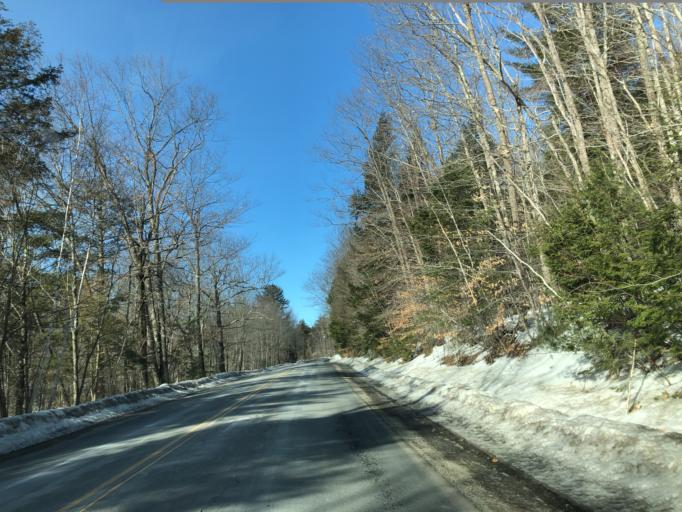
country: US
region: Maine
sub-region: Androscoggin County
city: Minot
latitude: 44.1462
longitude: -70.3297
